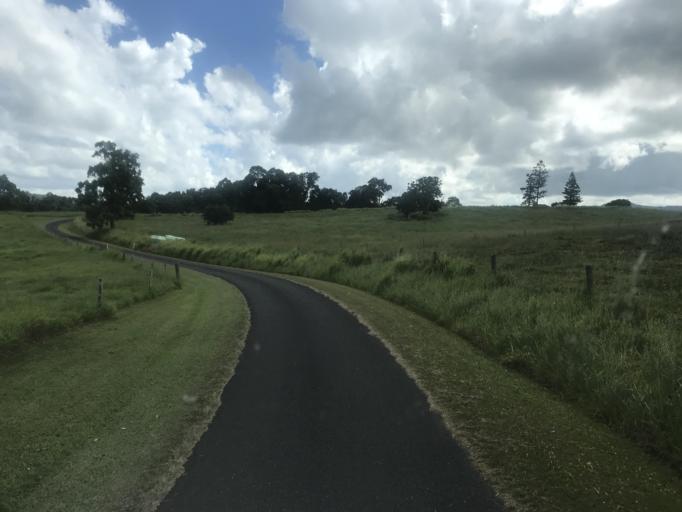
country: AU
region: Queensland
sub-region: Tablelands
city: Ravenshoe
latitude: -17.5555
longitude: 145.6906
